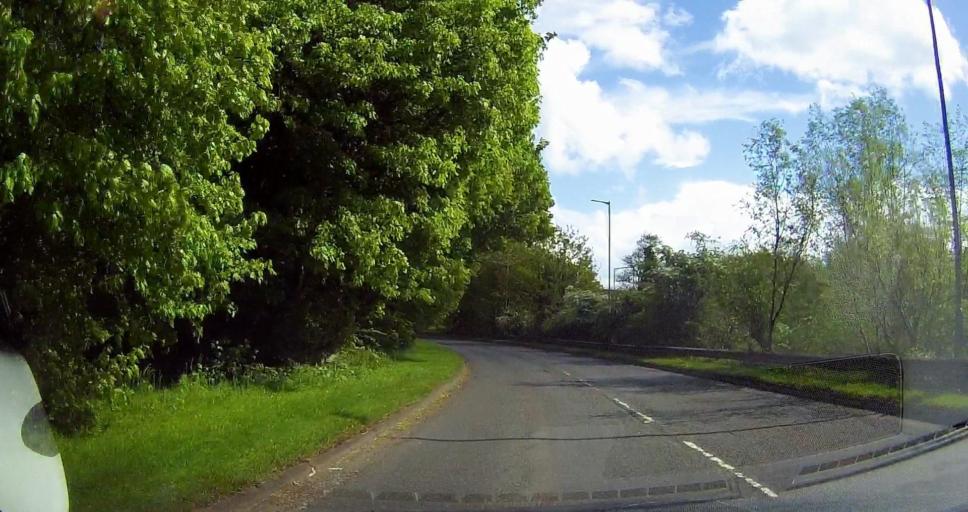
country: GB
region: Scotland
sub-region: Falkirk
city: Larbert
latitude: 56.0176
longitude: -3.8342
